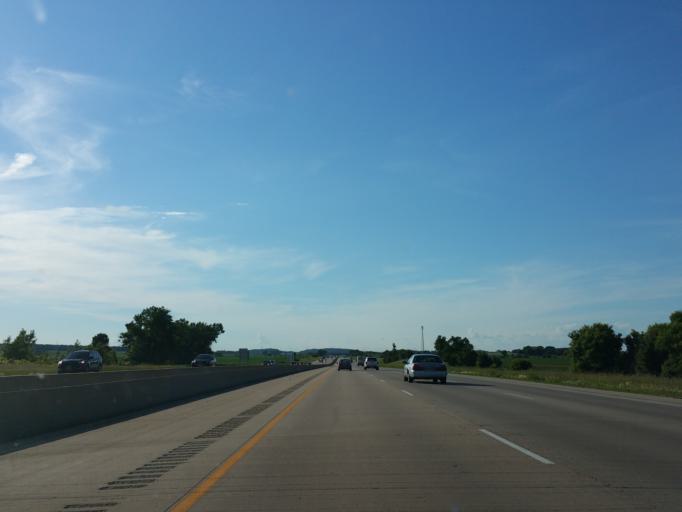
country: US
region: Wisconsin
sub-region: Dane County
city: De Forest
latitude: 43.2641
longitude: -89.3882
